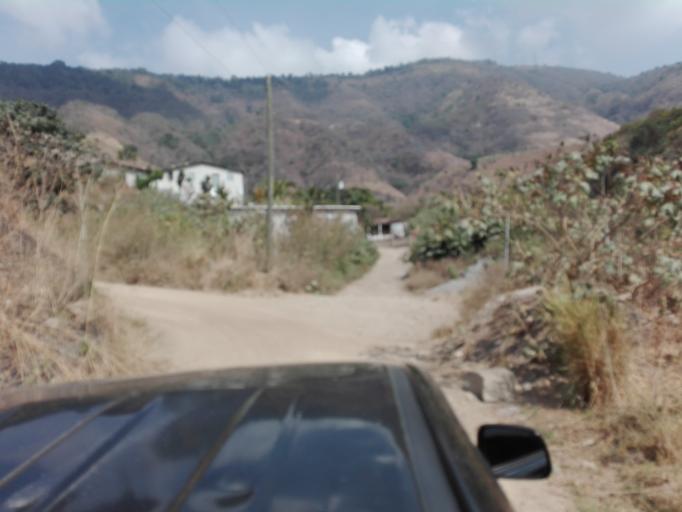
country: GT
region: Escuintla
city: San Vicente Pacaya
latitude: 14.4448
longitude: -90.6534
